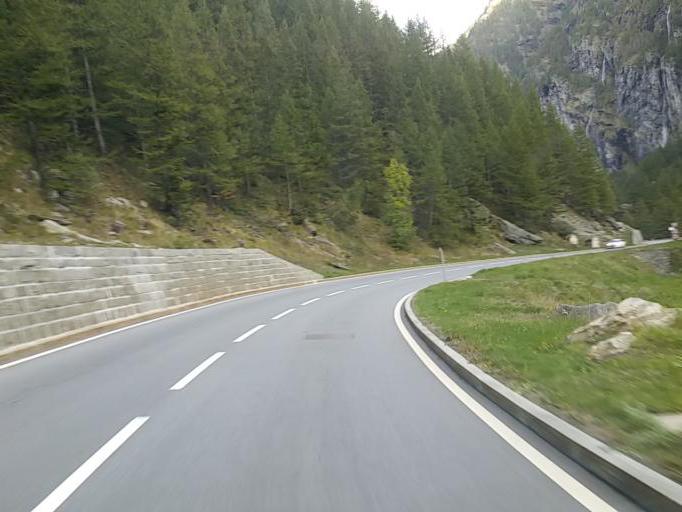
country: IT
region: Piedmont
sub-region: Provincia Verbano-Cusio-Ossola
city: Antronapiana
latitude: 46.1859
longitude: 8.0790
